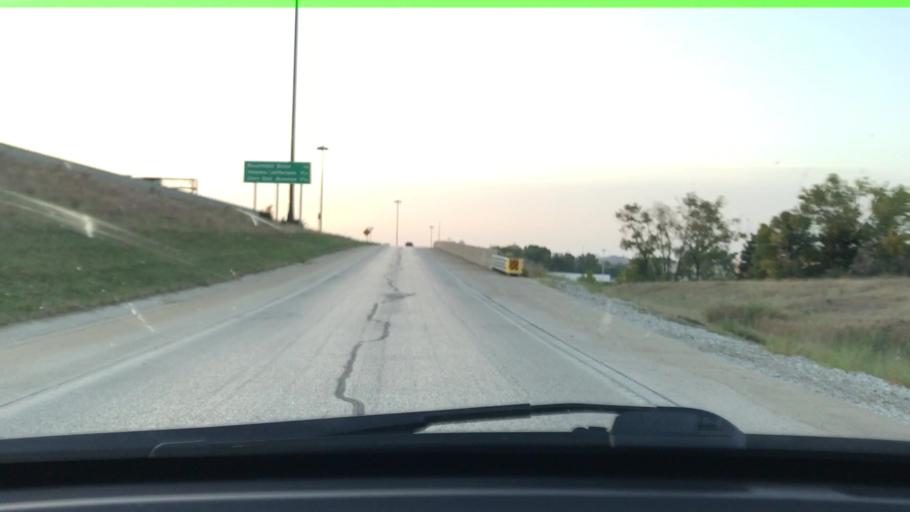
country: US
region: Illinois
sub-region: Tazewell County
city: East Peoria
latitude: 40.6712
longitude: -89.5737
